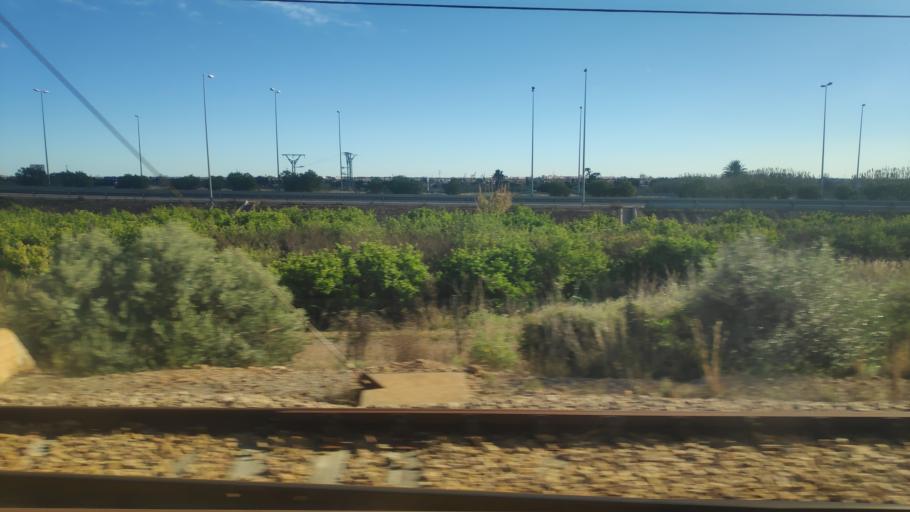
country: ES
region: Valencia
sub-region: Provincia de Castello
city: Castello de la Plana
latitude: 40.0218
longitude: -0.0058
